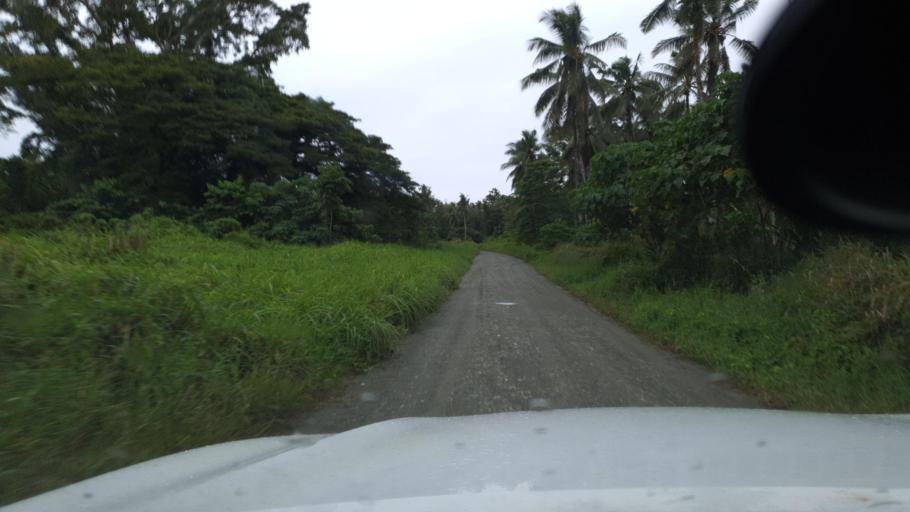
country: SB
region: Central Province
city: Tulaghi
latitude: -9.4527
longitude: 160.3910
